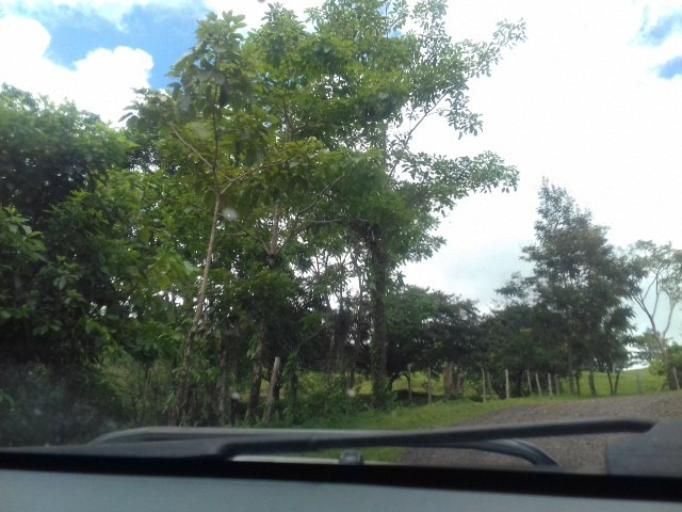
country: NI
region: Matagalpa
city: Rio Blanco
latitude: 12.9970
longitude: -85.1943
